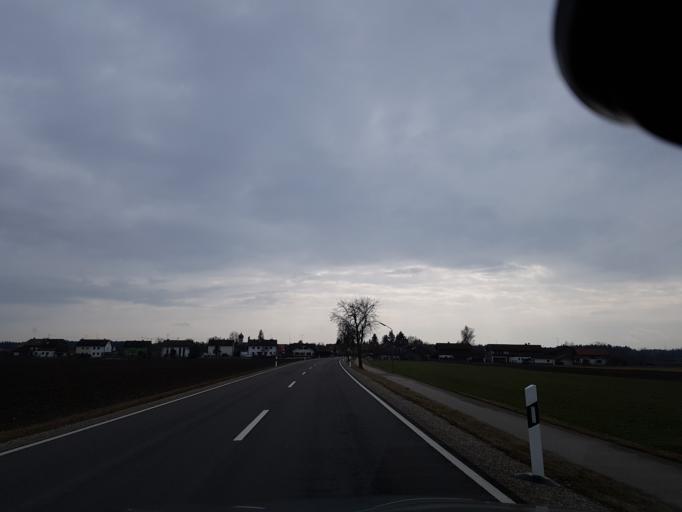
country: DE
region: Bavaria
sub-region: Upper Bavaria
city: Hohenkirchen-Siegertsbrunn
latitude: 47.9910
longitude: 11.7126
